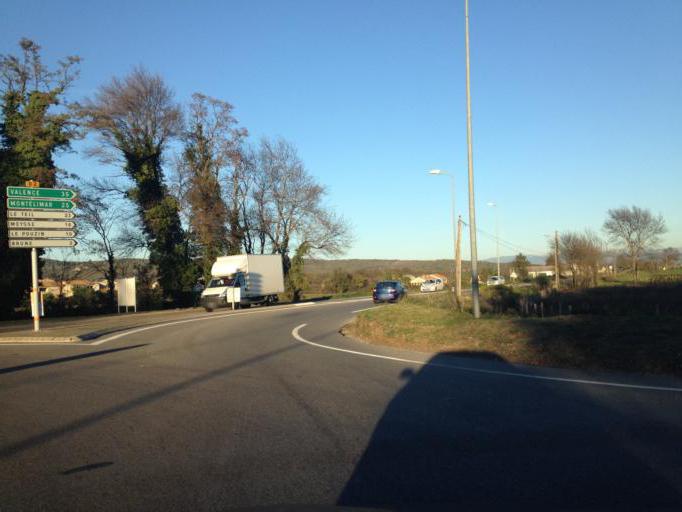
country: FR
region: Rhone-Alpes
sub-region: Departement de l'Ardeche
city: Chomerac
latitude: 44.7080
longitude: 4.6674
